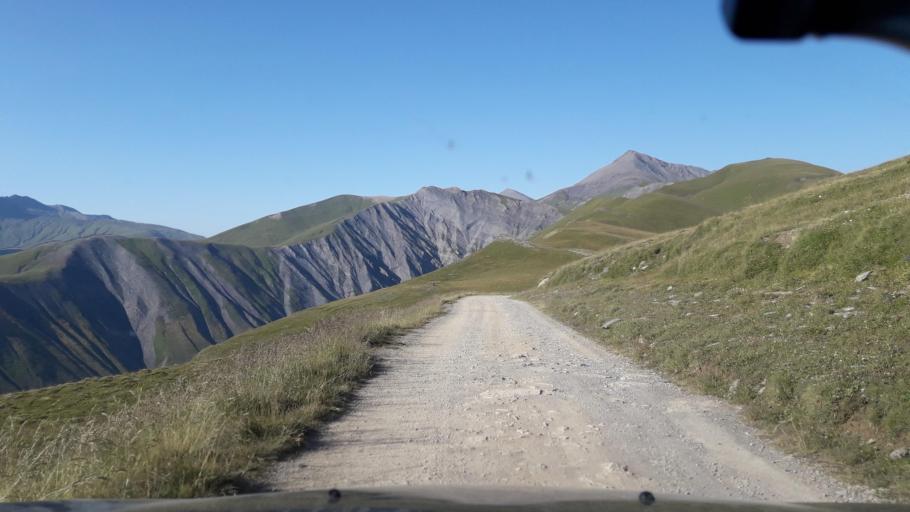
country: FR
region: Rhone-Alpes
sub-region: Departement de l'Isere
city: Mont-de-Lans
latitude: 45.0705
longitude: 6.2024
